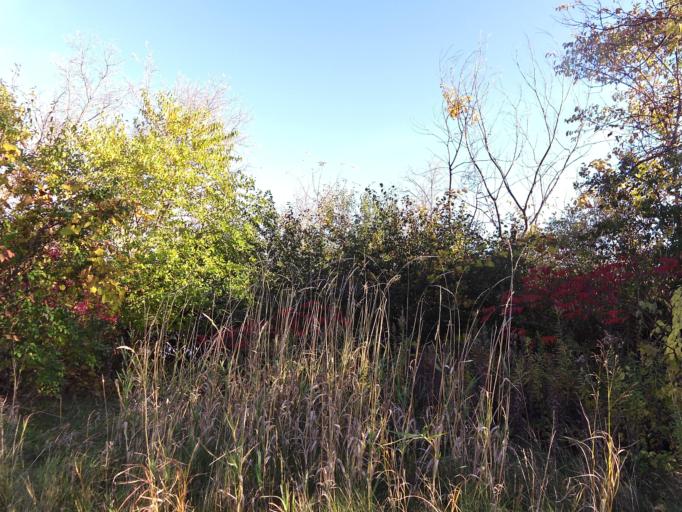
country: US
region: Minnesota
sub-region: Scott County
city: Prior Lake
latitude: 44.7016
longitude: -93.4420
